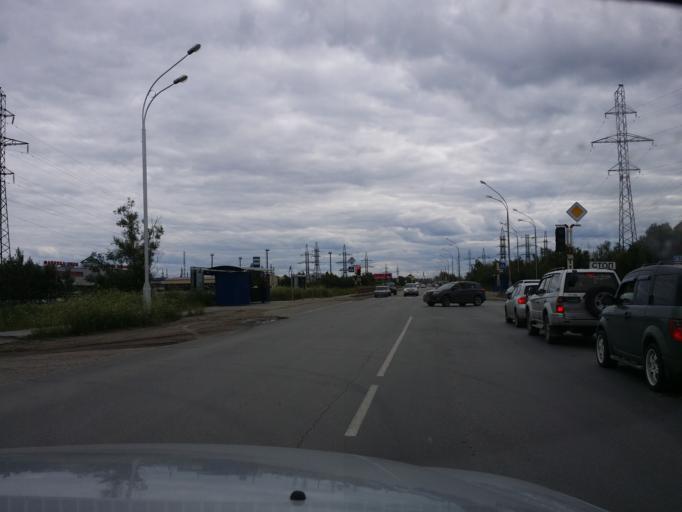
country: RU
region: Khanty-Mansiyskiy Avtonomnyy Okrug
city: Nizhnevartovsk
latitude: 60.9362
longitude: 76.5307
